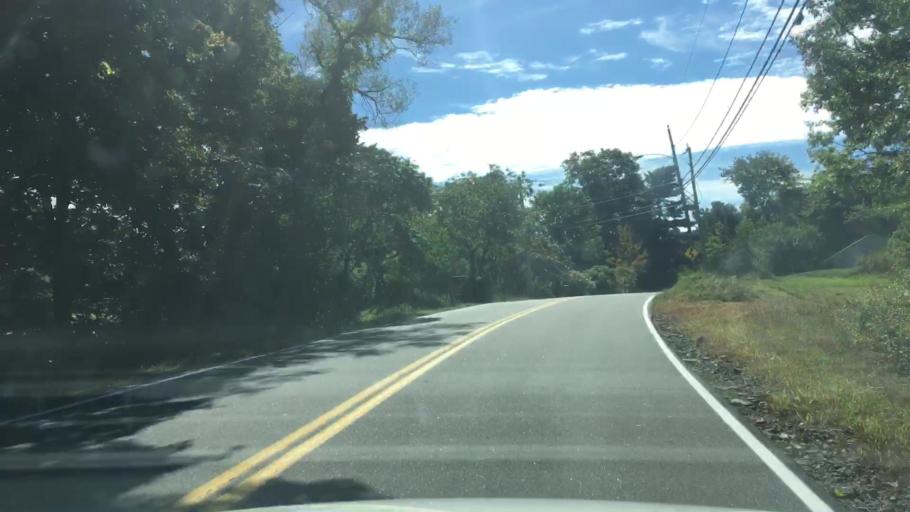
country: US
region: Maine
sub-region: York County
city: Kittery Point
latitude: 43.1014
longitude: -70.6755
